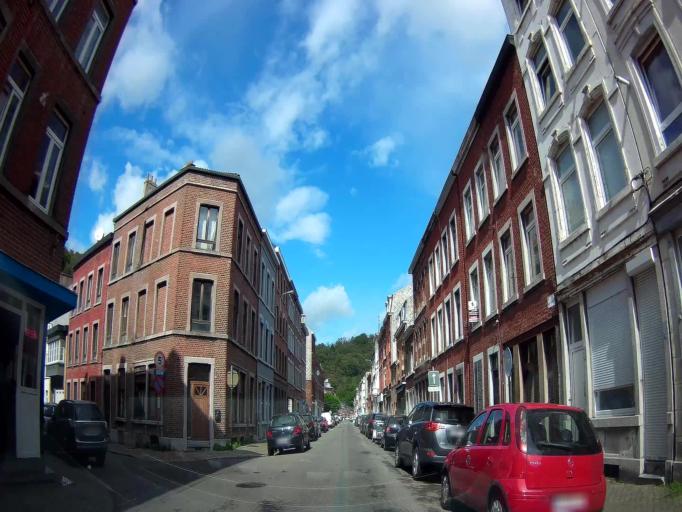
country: BE
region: Wallonia
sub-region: Province de Liege
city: Verviers
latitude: 50.5977
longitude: 5.8740
